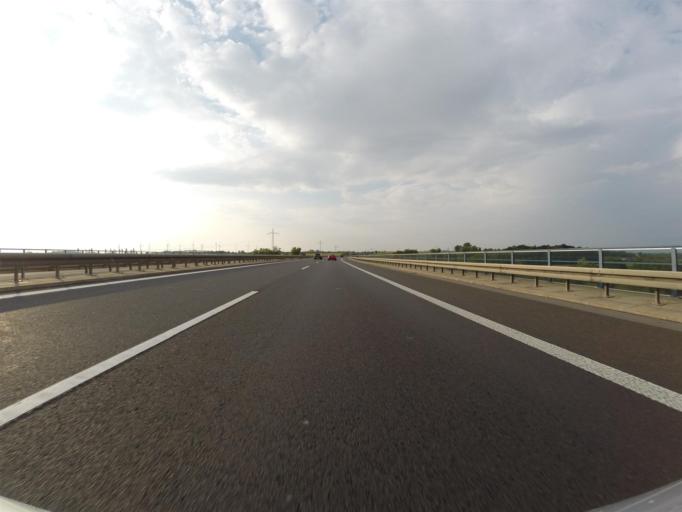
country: DE
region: Saxony-Anhalt
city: Grosskorbetha
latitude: 51.2431
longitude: 12.0268
